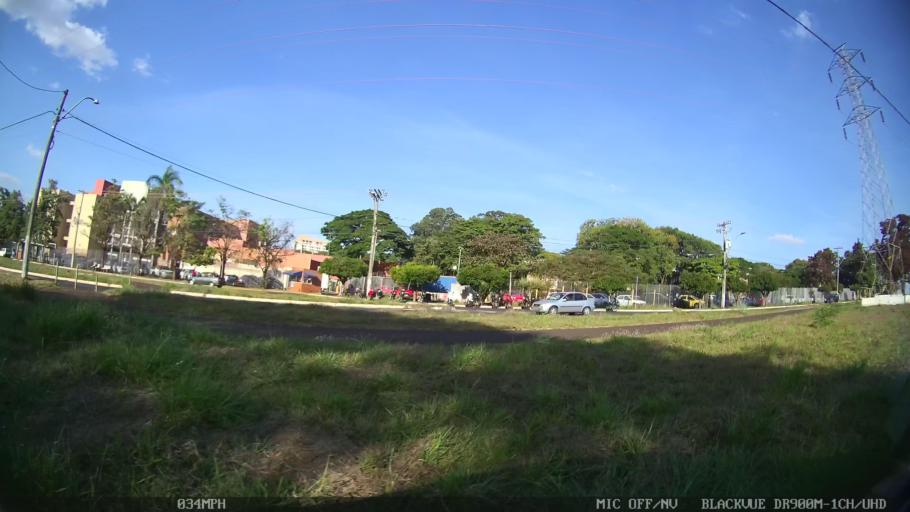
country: BR
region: Sao Paulo
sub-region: Ribeirao Preto
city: Ribeirao Preto
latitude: -21.2010
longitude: -47.7808
